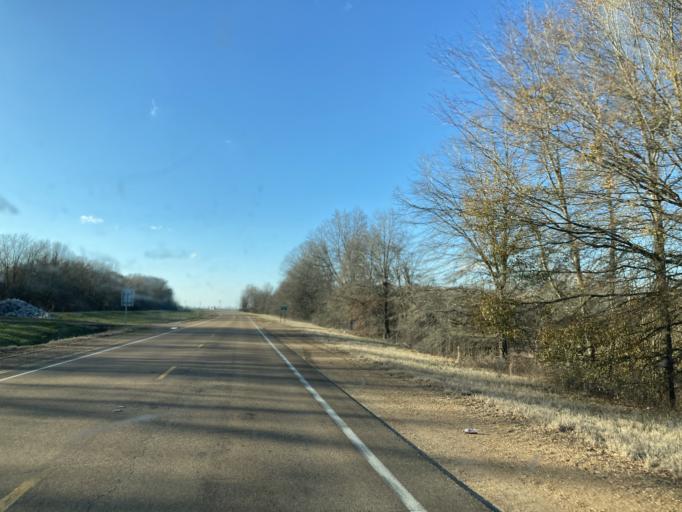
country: US
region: Mississippi
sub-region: Yazoo County
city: Yazoo City
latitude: 32.9228
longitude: -90.5664
